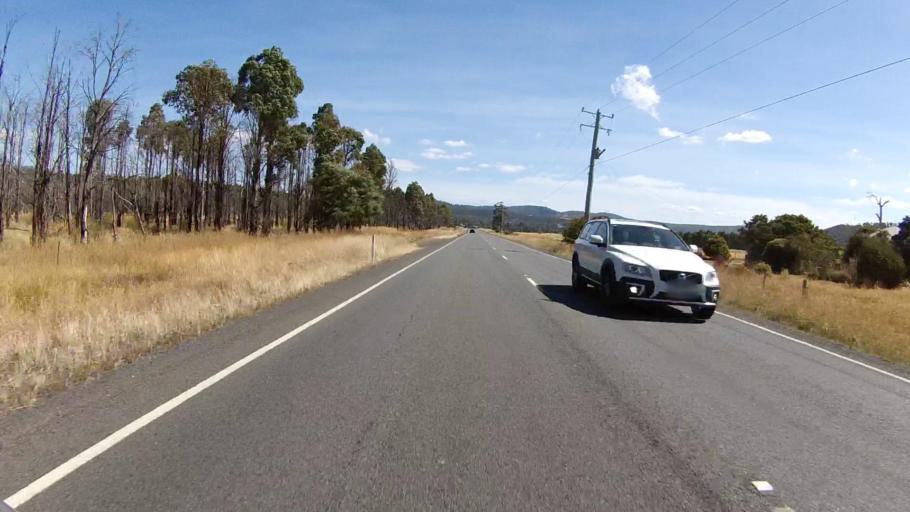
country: AU
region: Tasmania
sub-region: Sorell
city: Sorell
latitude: -42.6056
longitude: 147.7450
